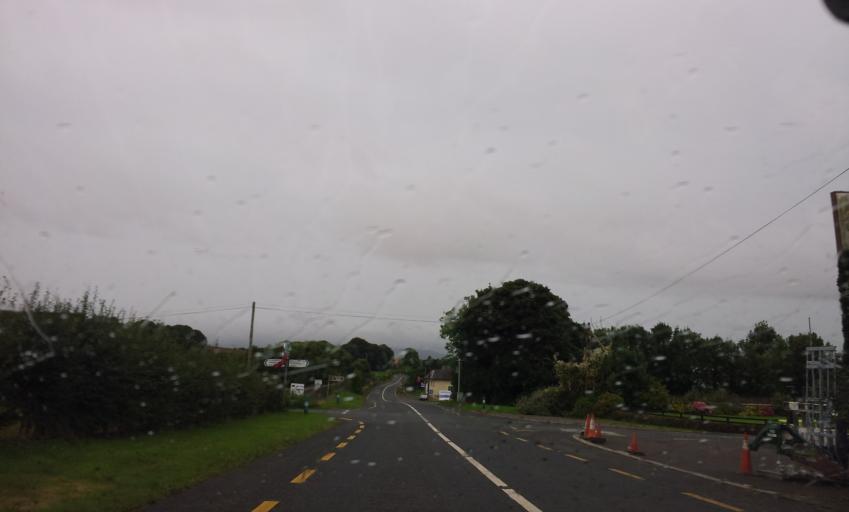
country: IE
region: Munster
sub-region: County Cork
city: Mallow
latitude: 52.2215
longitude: -8.5034
